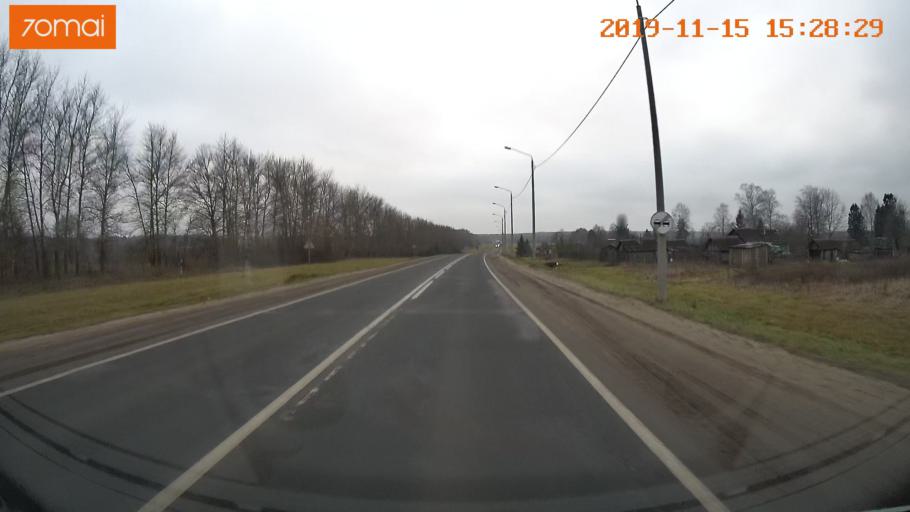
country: RU
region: Jaroslavl
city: Danilov
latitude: 58.1317
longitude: 40.1345
